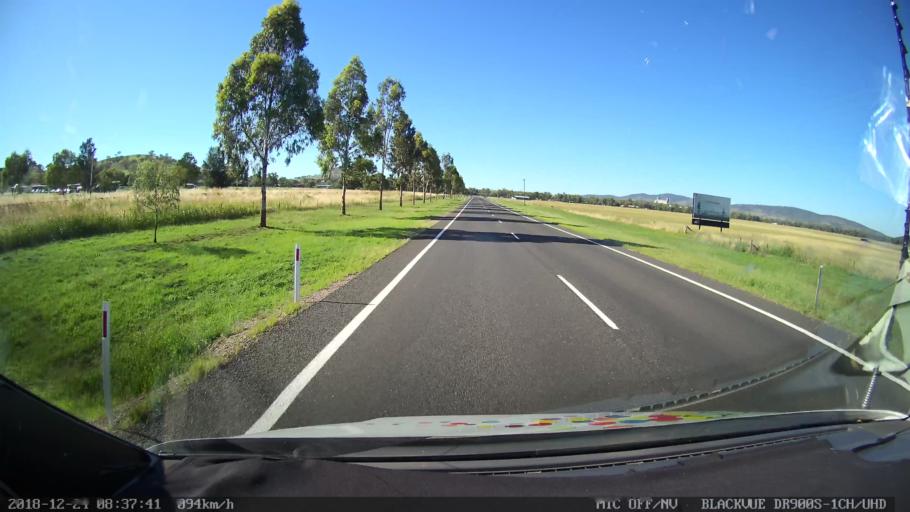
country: AU
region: New South Wales
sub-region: Liverpool Plains
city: Quirindi
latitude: -31.3323
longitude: 150.6484
